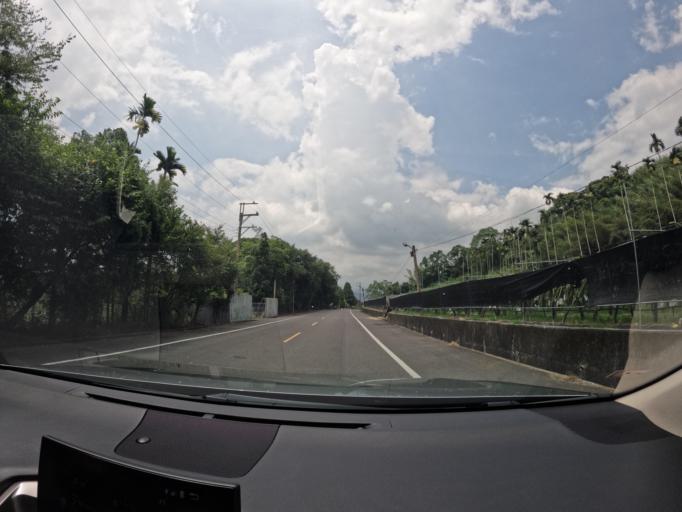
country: TW
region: Taiwan
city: Lugu
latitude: 23.8005
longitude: 120.7896
